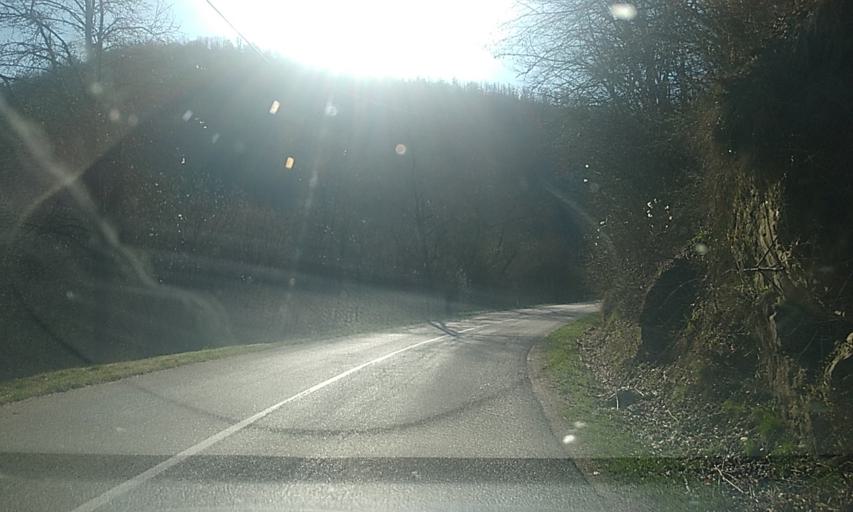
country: RS
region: Central Serbia
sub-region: Pcinjski Okrug
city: Bosilegrad
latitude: 42.4449
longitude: 22.5051
